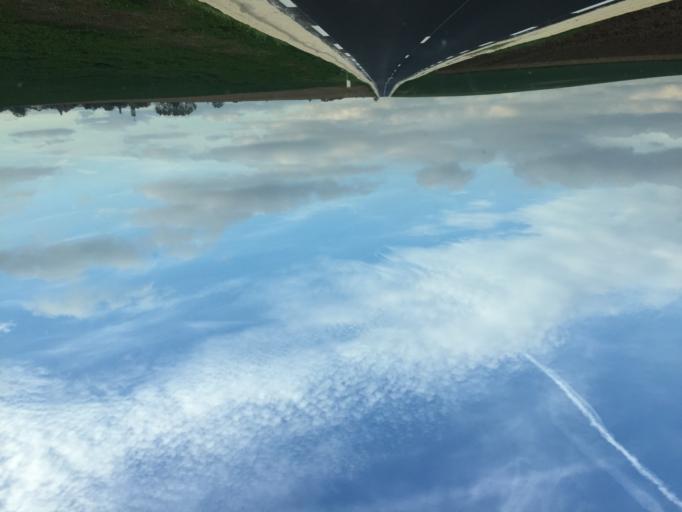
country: FR
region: Ile-de-France
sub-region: Departement de Seine-et-Marne
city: Saints
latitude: 48.6987
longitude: 3.0684
